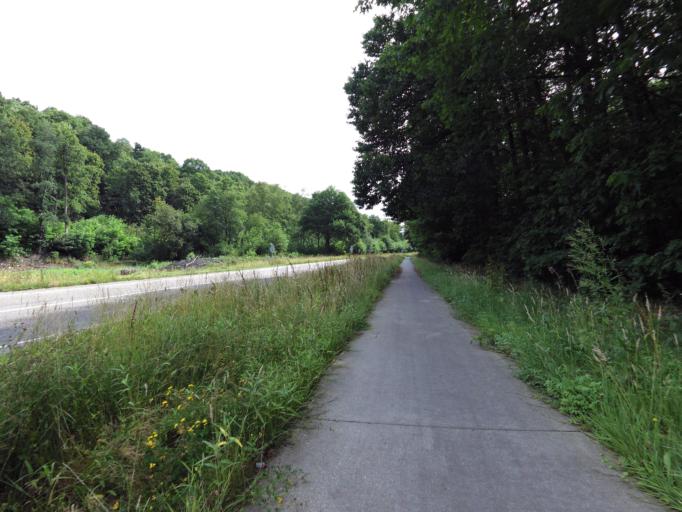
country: NL
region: Limburg
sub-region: Gemeente Brunssum
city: Brunssum
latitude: 50.9374
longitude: 5.9995
